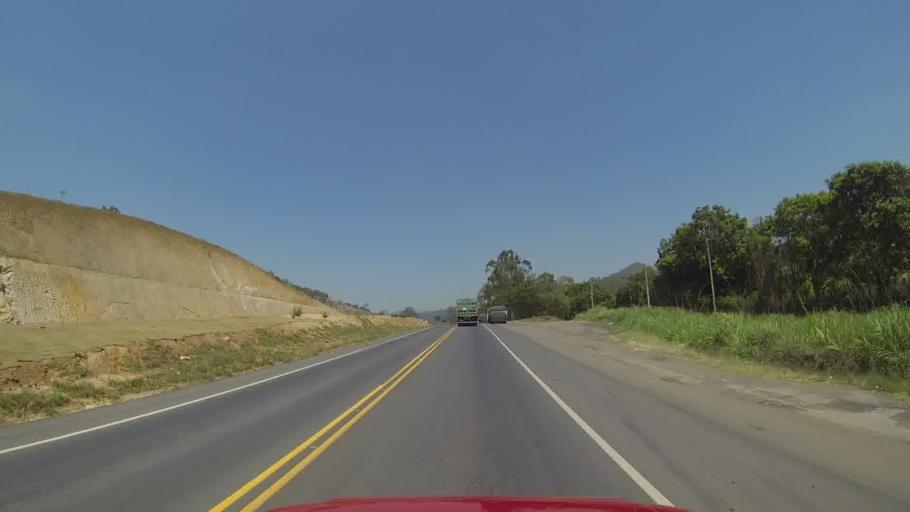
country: BR
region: Minas Gerais
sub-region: Mateus Leme
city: Mateus Leme
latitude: -20.0137
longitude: -44.4841
